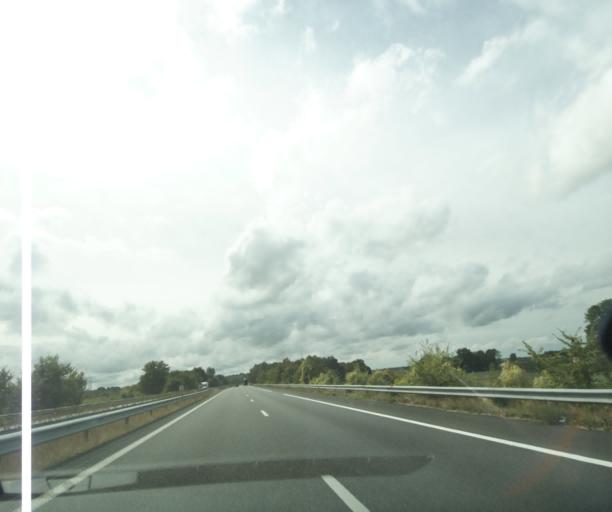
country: FR
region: Poitou-Charentes
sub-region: Departement de la Charente-Maritime
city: Saint-Genis-de-Saintonge
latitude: 45.5004
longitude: -0.6134
